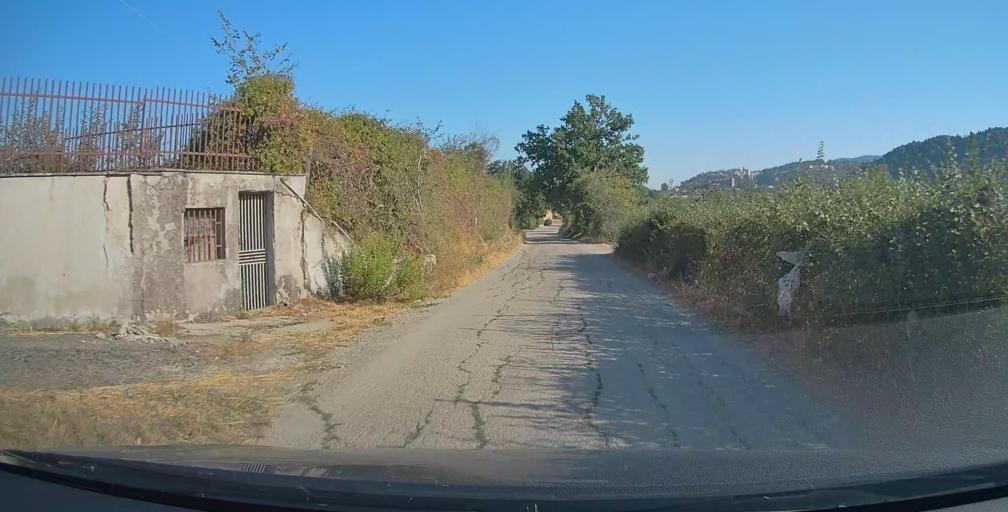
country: IT
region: Umbria
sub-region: Provincia di Terni
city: Calvi dell'Umbria
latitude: 42.3851
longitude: 12.5685
